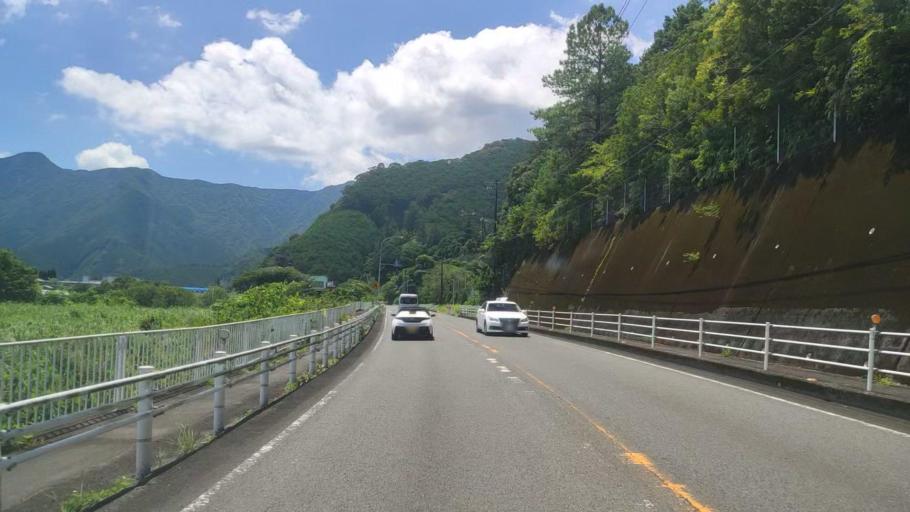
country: JP
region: Mie
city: Owase
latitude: 34.1433
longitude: 136.2257
